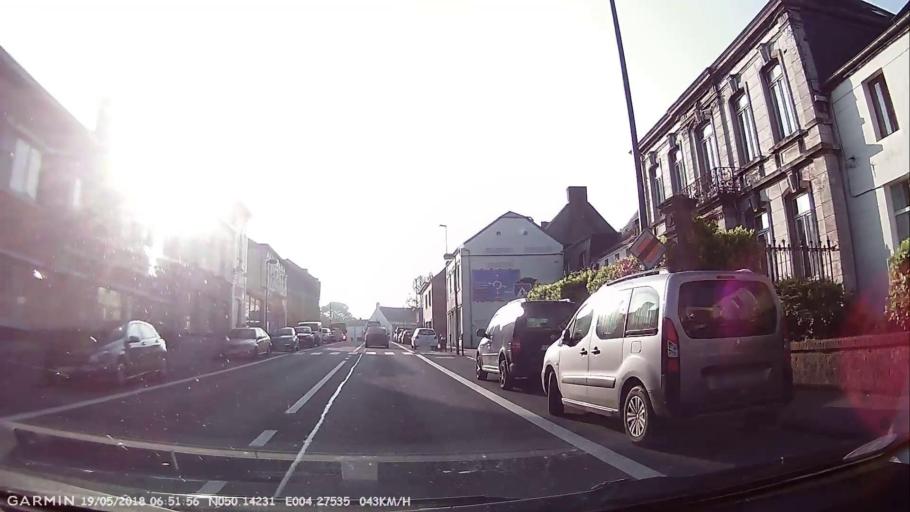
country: BE
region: Wallonia
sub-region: Province du Hainaut
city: Froidchapelle
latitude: 50.1423
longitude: 4.2755
